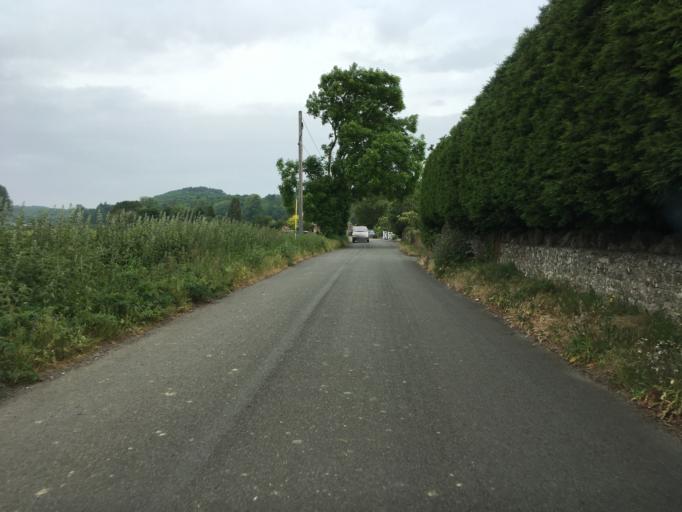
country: GB
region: England
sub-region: North Somerset
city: Clevedon
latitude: 51.4535
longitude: -2.8223
